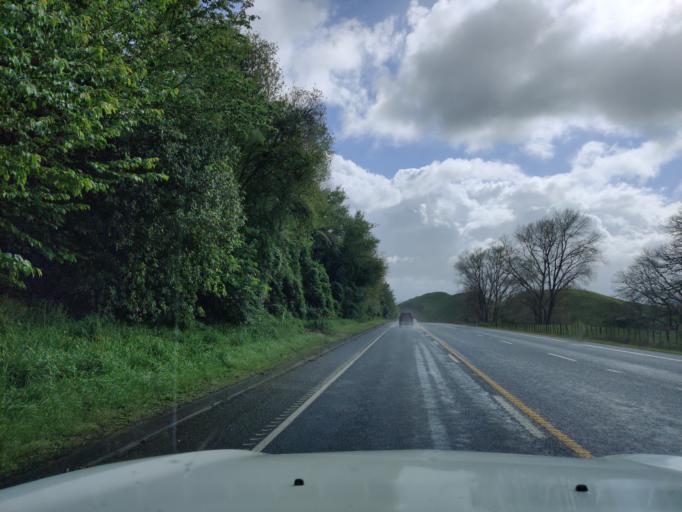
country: NZ
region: Waikato
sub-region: Matamata-Piako District
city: Matamata
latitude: -37.9798
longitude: 175.7380
